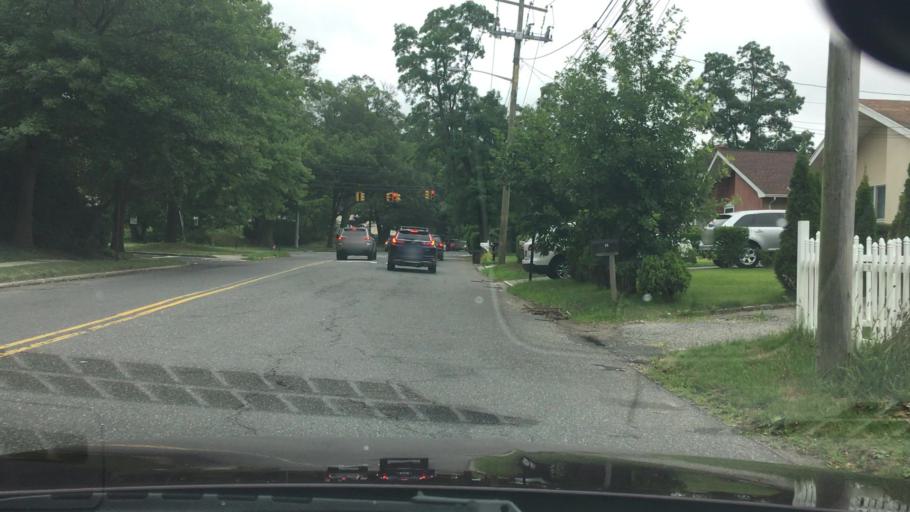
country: US
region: New York
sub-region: Suffolk County
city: South Huntington
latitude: 40.8140
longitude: -73.4086
